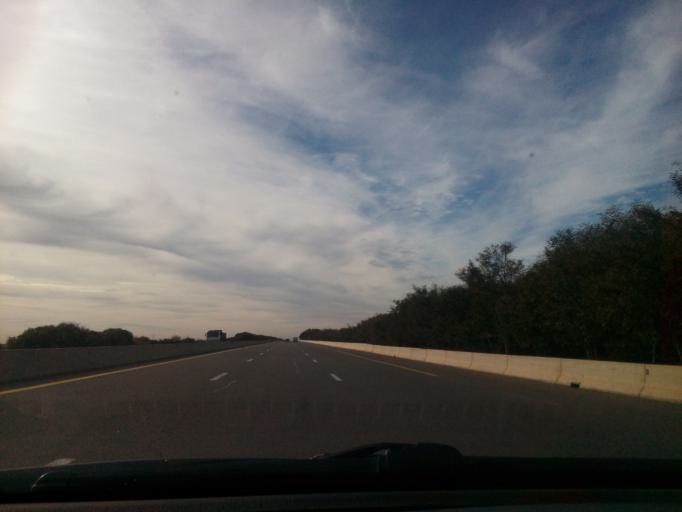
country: DZ
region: Sidi Bel Abbes
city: Sidi Bel Abbes
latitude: 35.2057
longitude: -0.6886
